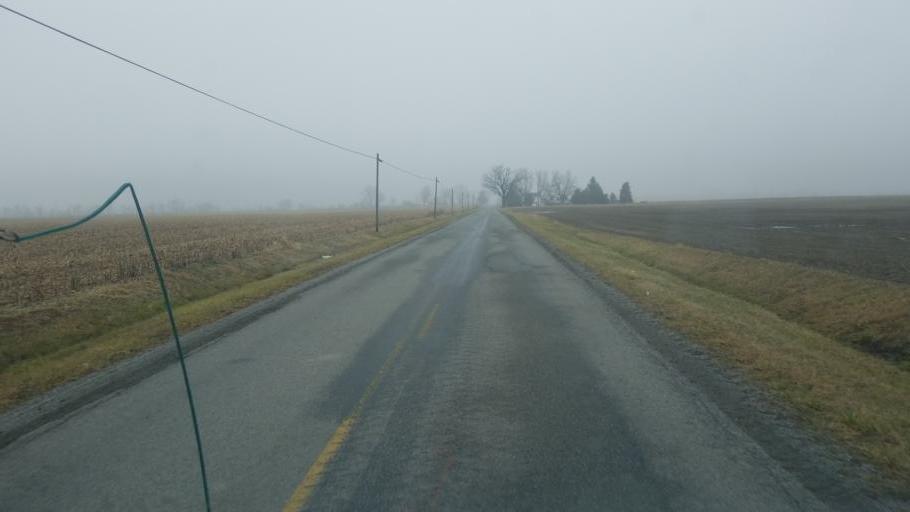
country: US
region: Ohio
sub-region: Hardin County
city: Kenton
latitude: 40.5131
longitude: -83.5224
